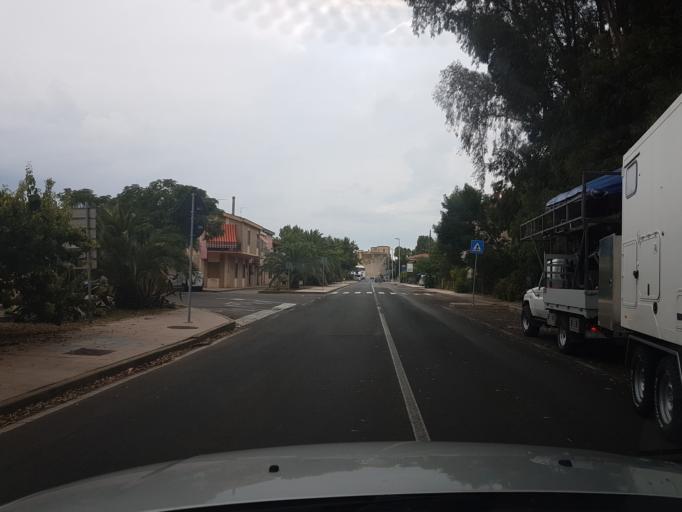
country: IT
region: Sardinia
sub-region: Provincia di Oristano
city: Cabras
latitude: 39.9077
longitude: 8.5198
